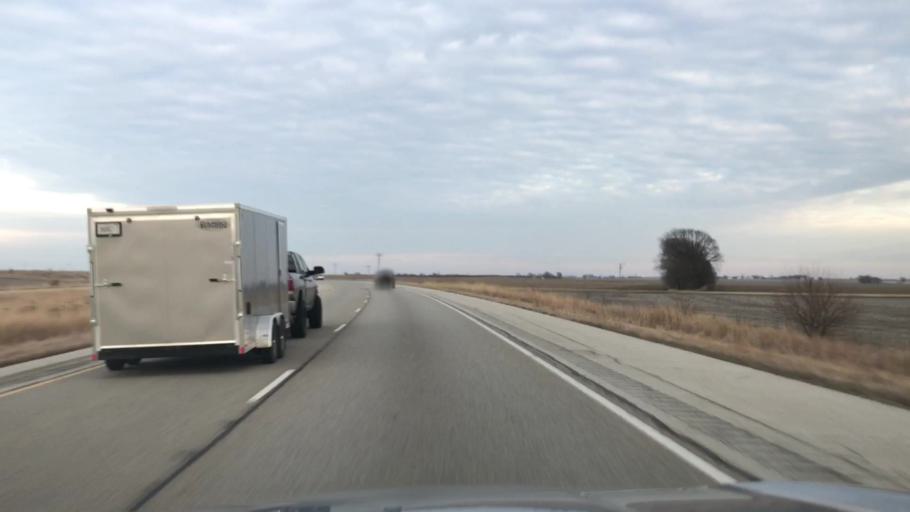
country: US
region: Illinois
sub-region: McLean County
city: Twin Grove
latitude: 40.3964
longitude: -89.0653
